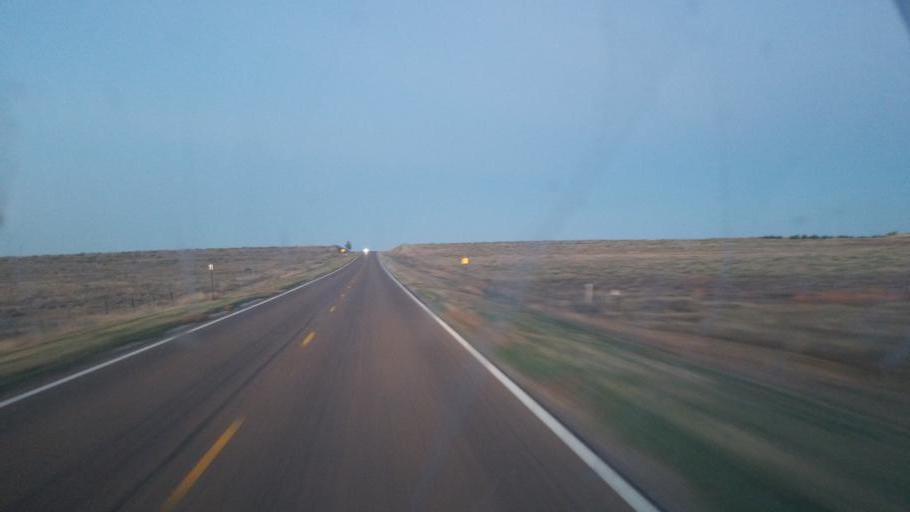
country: US
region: Kansas
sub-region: Wallace County
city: Sharon Springs
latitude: 39.0164
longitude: -101.3513
